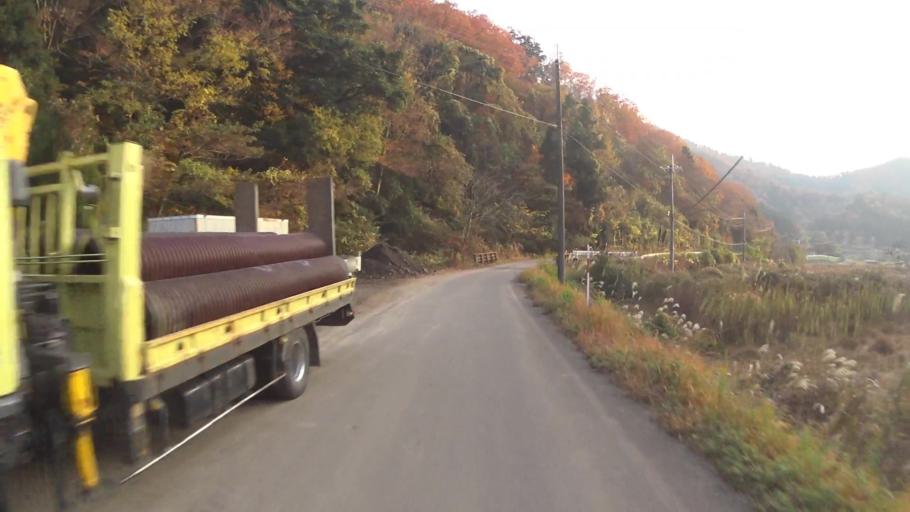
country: JP
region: Kyoto
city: Maizuru
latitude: 35.4901
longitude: 135.4658
